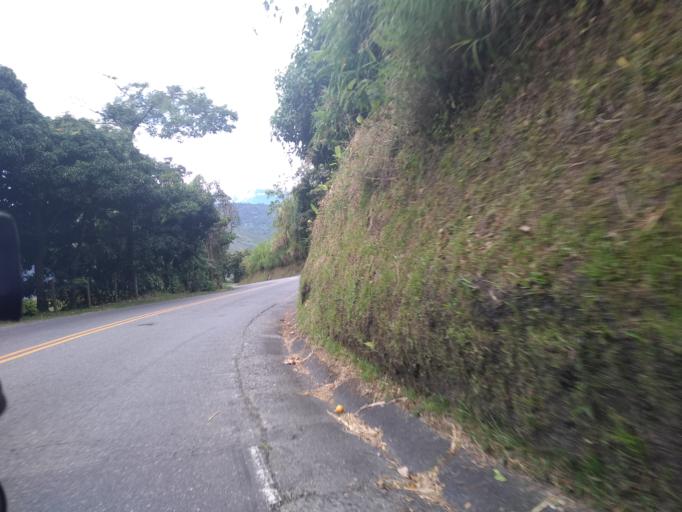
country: CO
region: Cauca
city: Rosas
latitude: 2.2442
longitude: -76.7681
